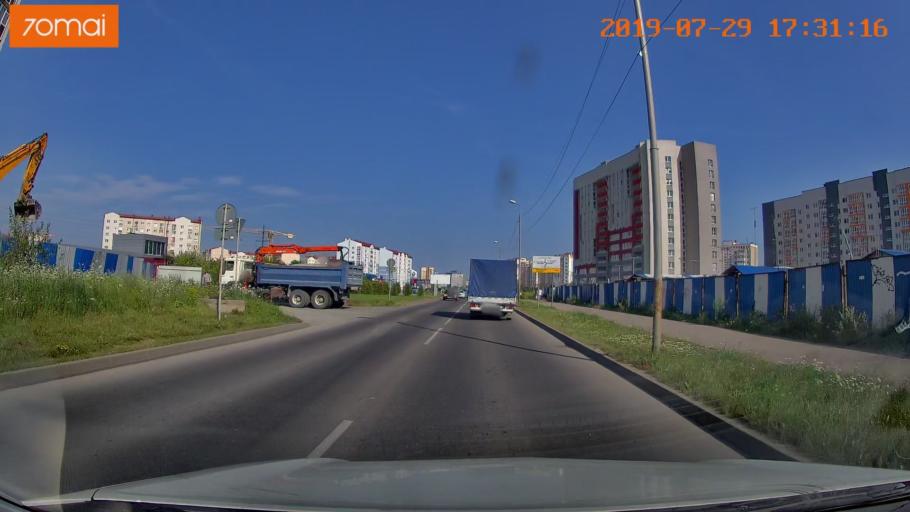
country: RU
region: Kaliningrad
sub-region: Gorod Kaliningrad
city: Kaliningrad
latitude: 54.7477
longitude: 20.4860
